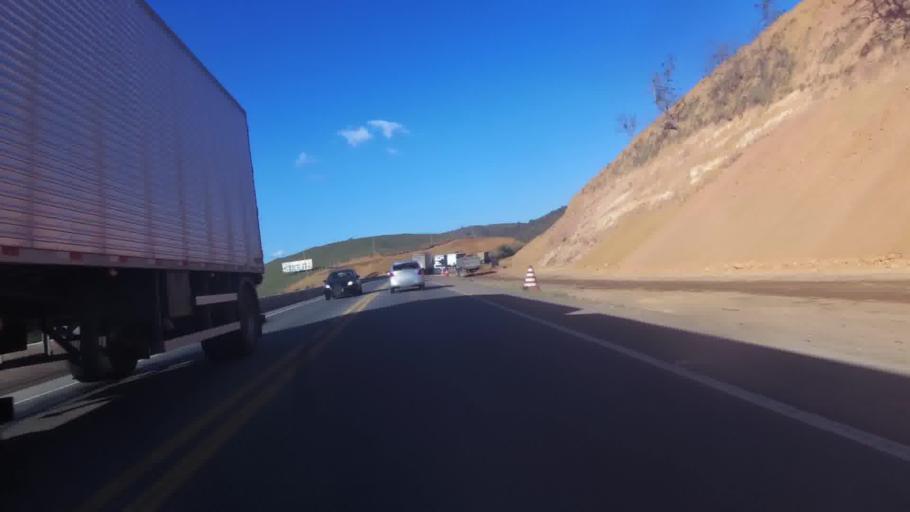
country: BR
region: Espirito Santo
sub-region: Iconha
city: Iconha
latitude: -20.7346
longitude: -40.7571
